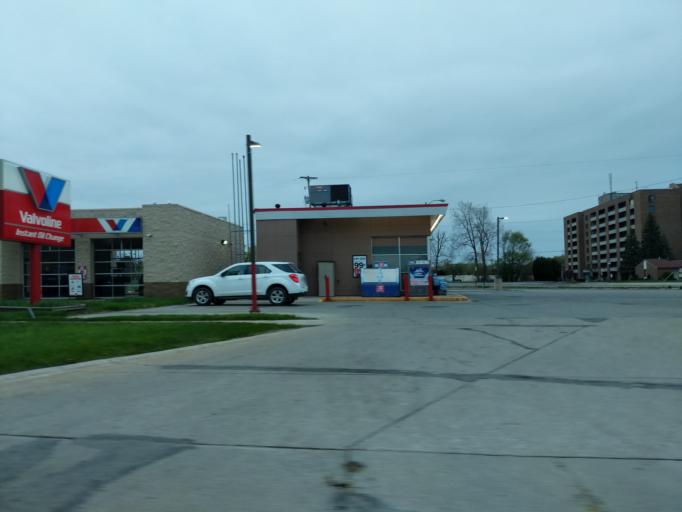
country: US
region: Michigan
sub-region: Midland County
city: Midland
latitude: 43.6181
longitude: -84.2179
